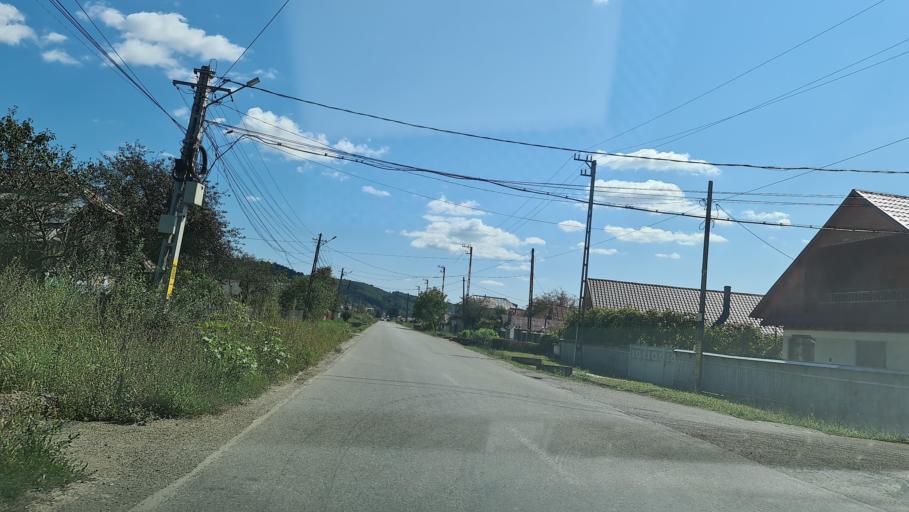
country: RO
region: Bacau
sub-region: Comuna Sanduleni
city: Sanduleni
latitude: 46.4485
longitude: 26.7294
